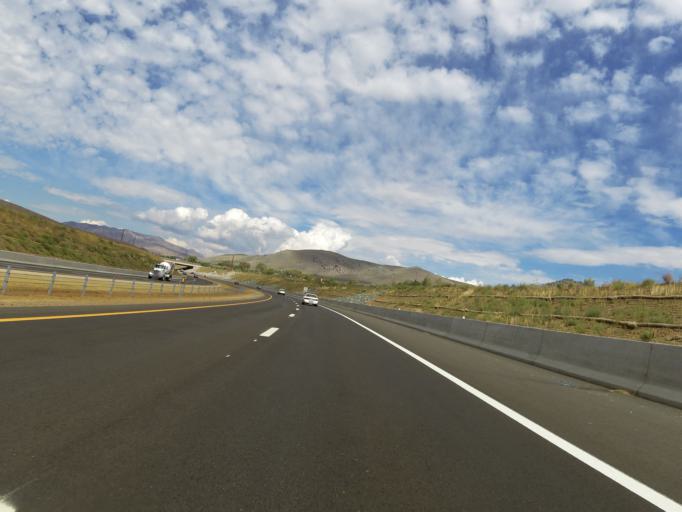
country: US
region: Nevada
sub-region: Carson City
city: Carson City
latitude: 39.1242
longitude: -119.7485
